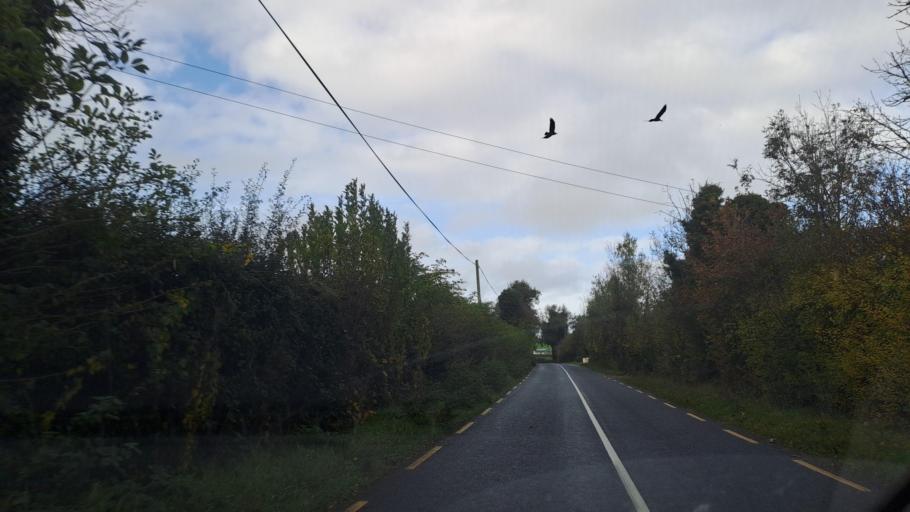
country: IE
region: Ulster
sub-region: County Monaghan
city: Carrickmacross
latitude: 53.9140
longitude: -6.7081
